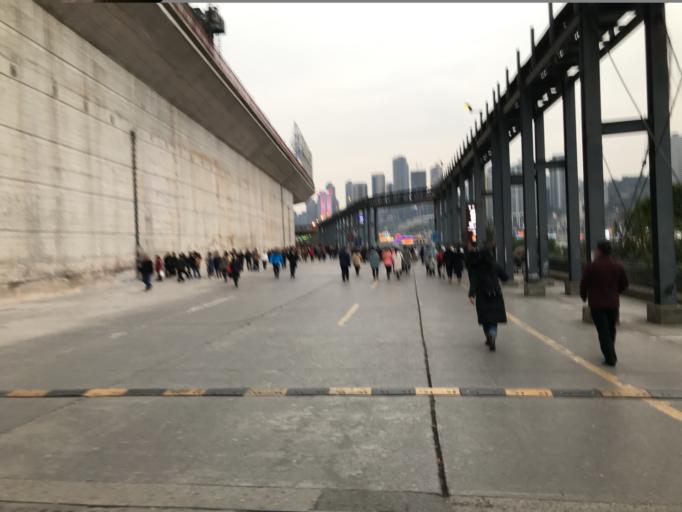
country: CN
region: Chongqing Shi
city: Nanping
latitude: 29.5671
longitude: 106.5854
